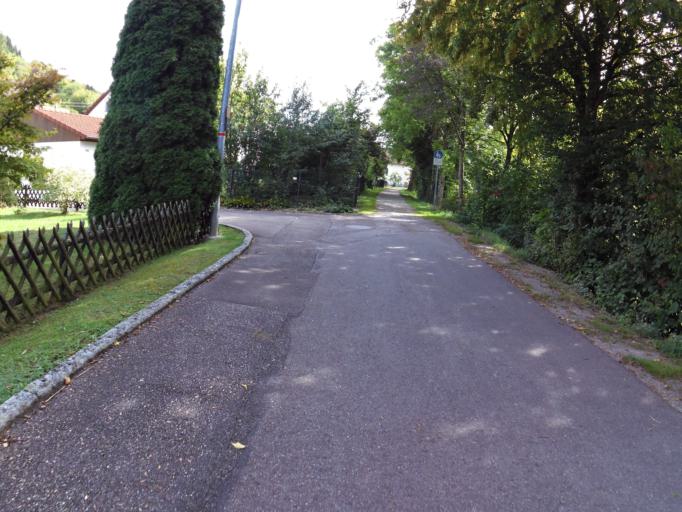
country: DE
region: Baden-Wuerttemberg
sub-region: Freiburg Region
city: Oberndorf
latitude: 48.3103
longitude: 8.5720
